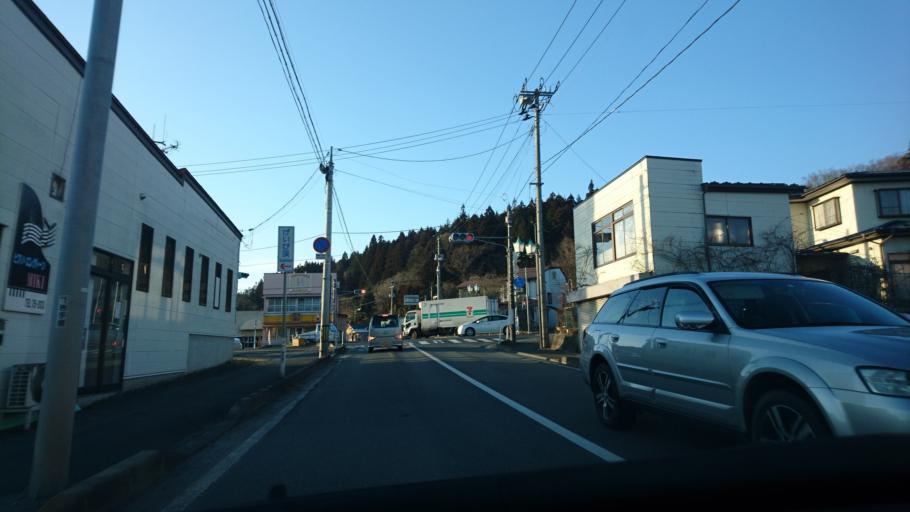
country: JP
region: Iwate
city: Ichinoseki
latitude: 38.9953
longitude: 141.3271
